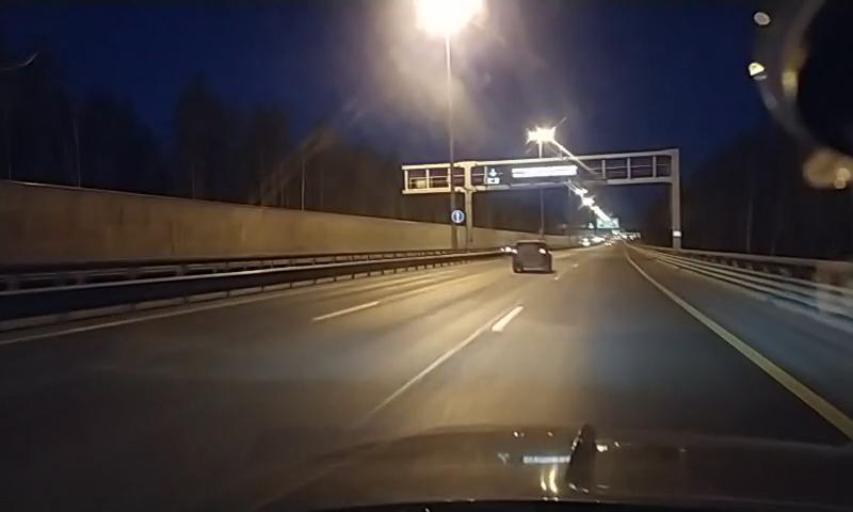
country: RU
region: St.-Petersburg
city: Beloostrov
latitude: 60.1191
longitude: 30.0740
